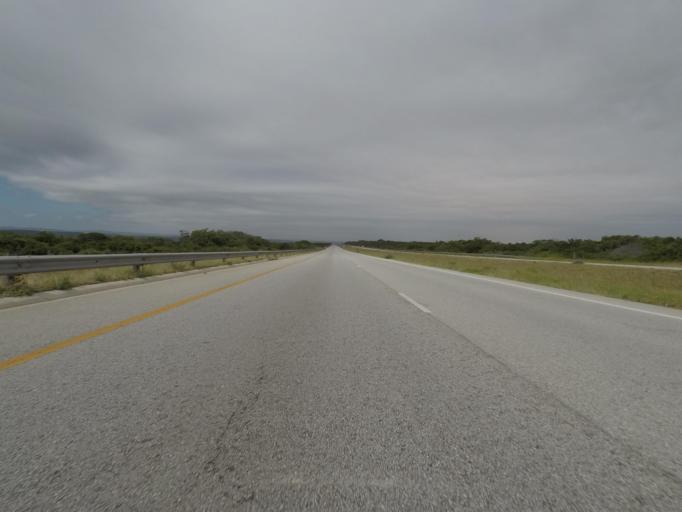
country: ZA
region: Eastern Cape
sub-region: Nelson Mandela Bay Metropolitan Municipality
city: Port Elizabeth
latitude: -33.7209
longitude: 25.7773
